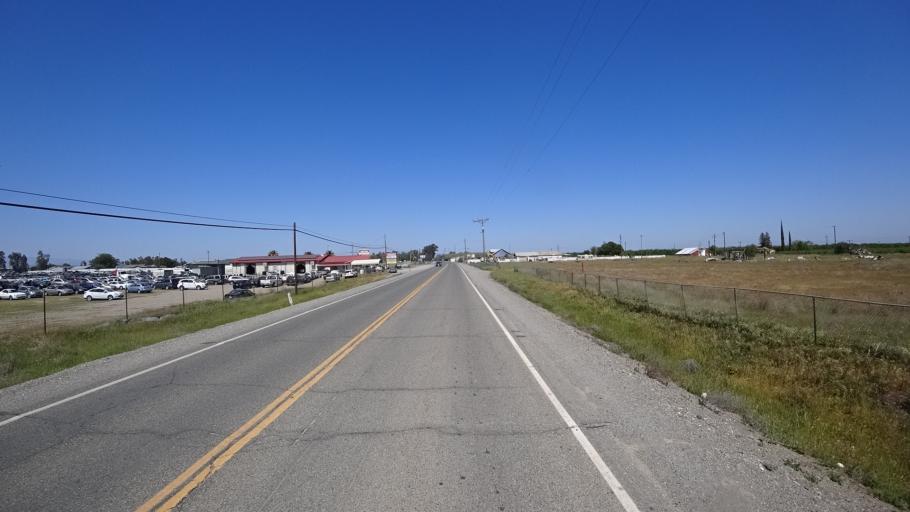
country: US
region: California
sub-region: Glenn County
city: Orland
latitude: 39.6953
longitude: -122.1965
